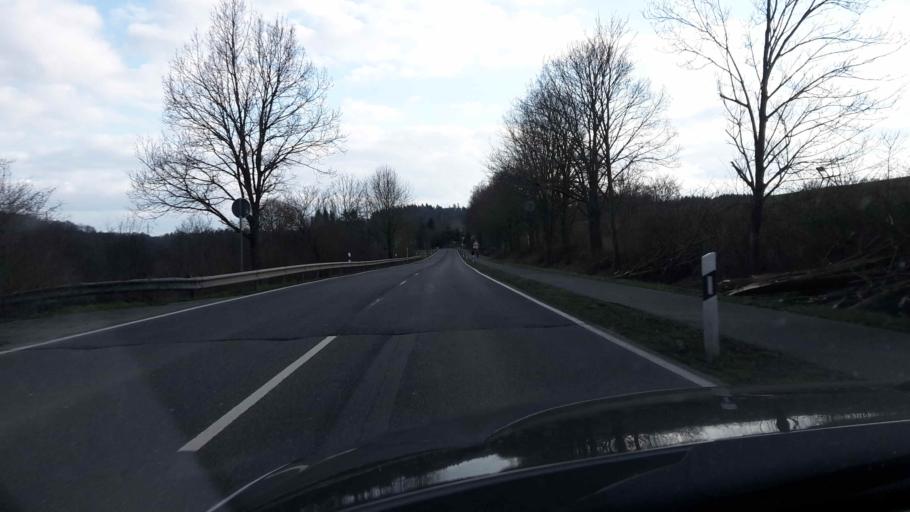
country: DE
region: North Rhine-Westphalia
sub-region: Regierungsbezirk Koln
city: Hennef
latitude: 50.6999
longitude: 7.2886
